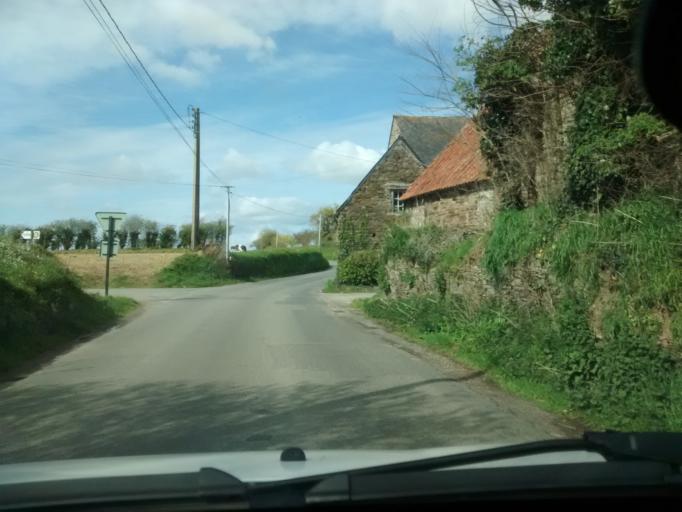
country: FR
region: Brittany
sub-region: Departement des Cotes-d'Armor
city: Langoat
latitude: 48.7680
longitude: -3.2790
